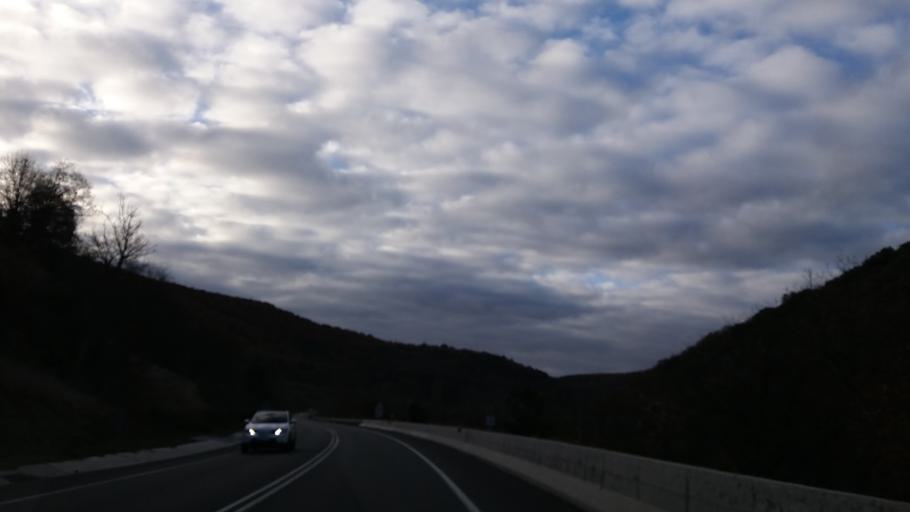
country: ES
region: Catalonia
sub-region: Provincia de Lleida
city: la Seu d'Urgell
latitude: 42.3865
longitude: 1.4601
